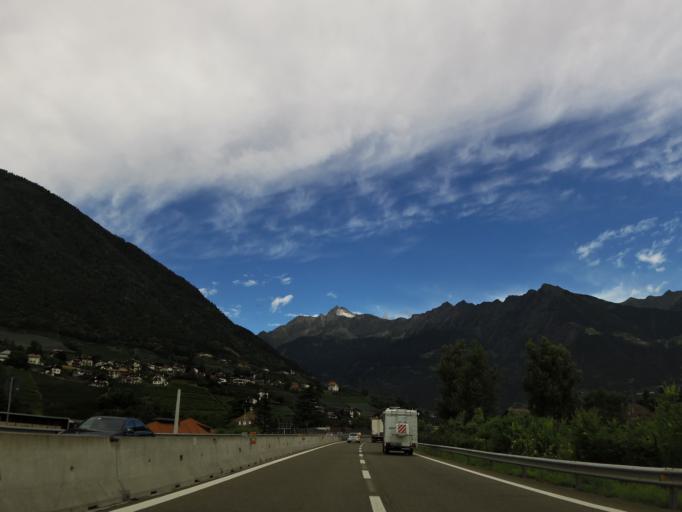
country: IT
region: Trentino-Alto Adige
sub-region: Bolzano
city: Marlengo
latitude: 46.6544
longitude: 11.1488
